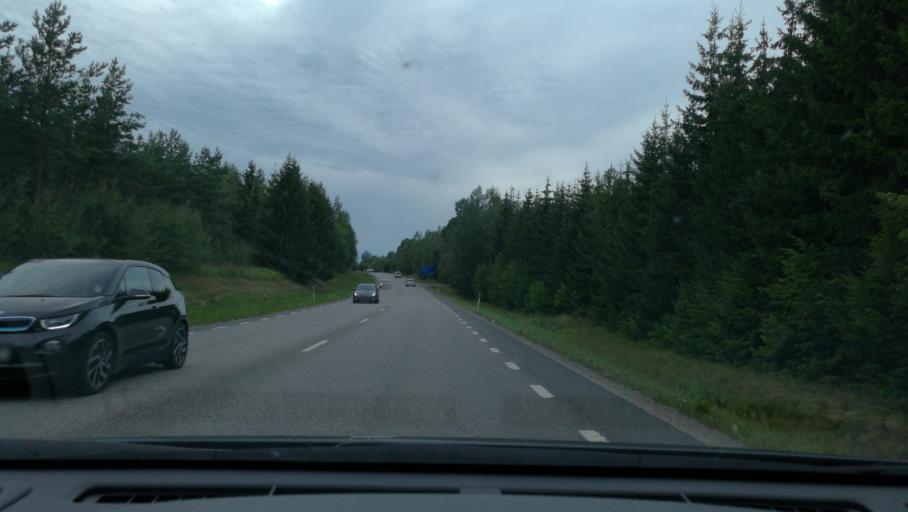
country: SE
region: Soedermanland
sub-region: Katrineholms Kommun
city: Katrineholm
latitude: 59.0080
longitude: 16.2222
